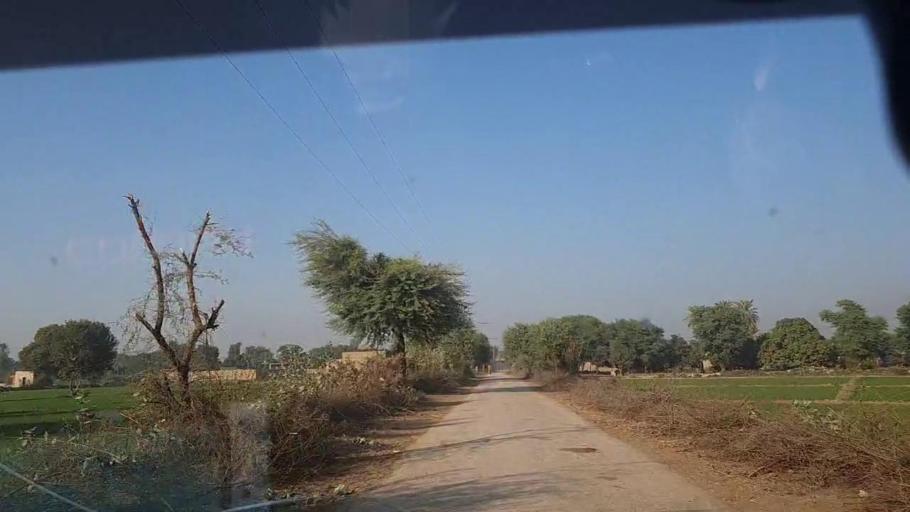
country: PK
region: Sindh
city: Sobhadero
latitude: 27.2531
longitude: 68.3505
